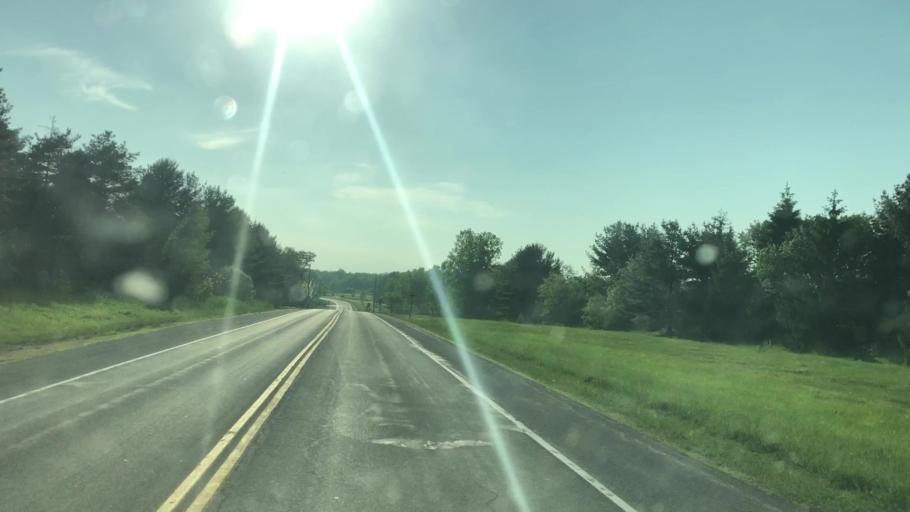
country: US
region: New York
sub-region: Wayne County
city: Macedon
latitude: 43.1224
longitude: -77.3180
